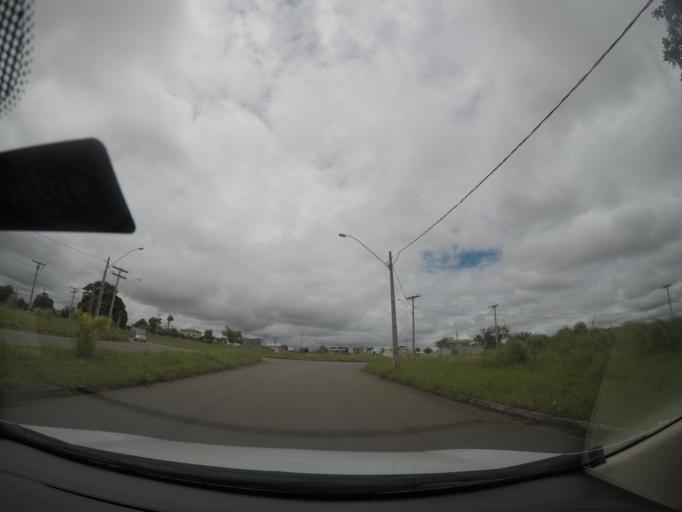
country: BR
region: Goias
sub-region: Goiania
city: Goiania
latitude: -16.7476
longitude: -49.3376
